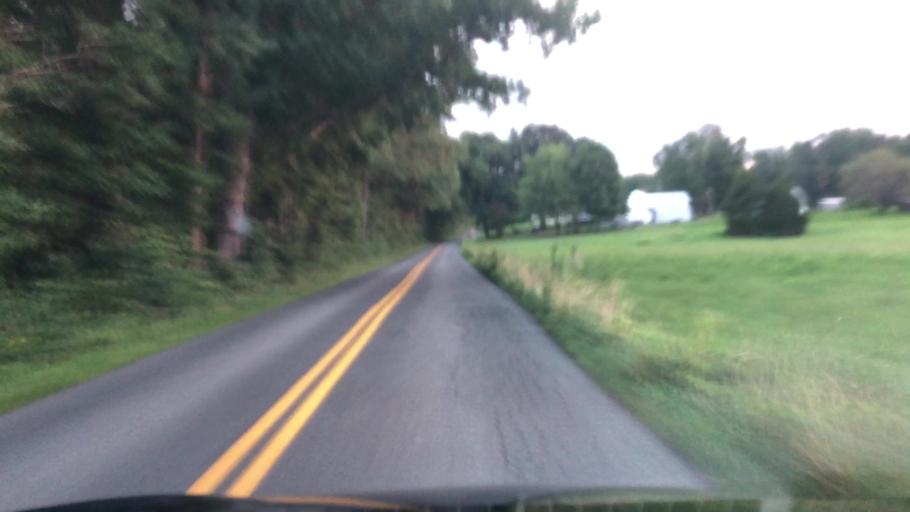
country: US
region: Virginia
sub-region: Stafford County
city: Stafford
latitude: 38.4609
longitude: -77.5778
